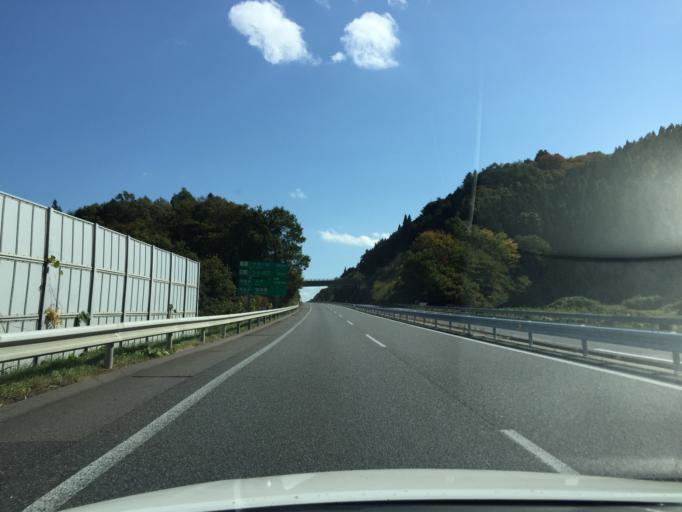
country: JP
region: Fukushima
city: Funehikimachi-funehiki
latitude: 37.2787
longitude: 140.6207
